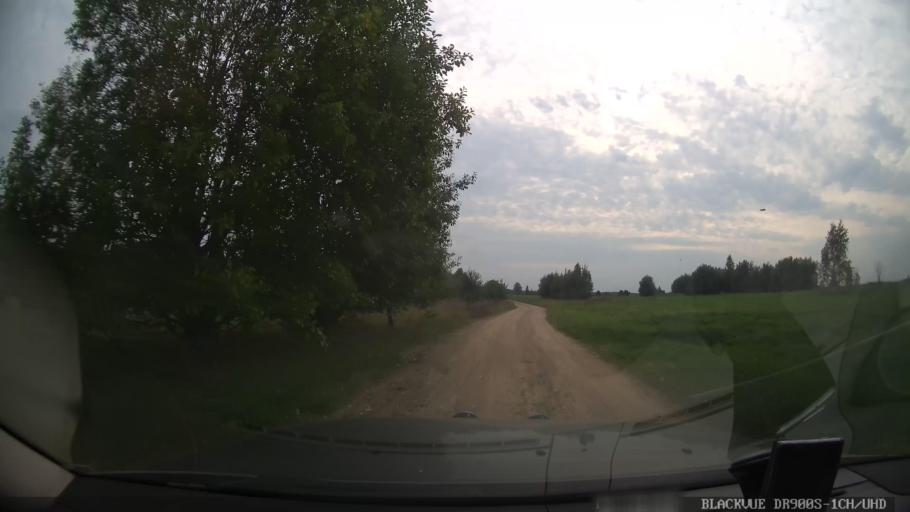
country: BY
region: Grodnenskaya
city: Ashmyany
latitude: 54.5346
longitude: 25.6727
